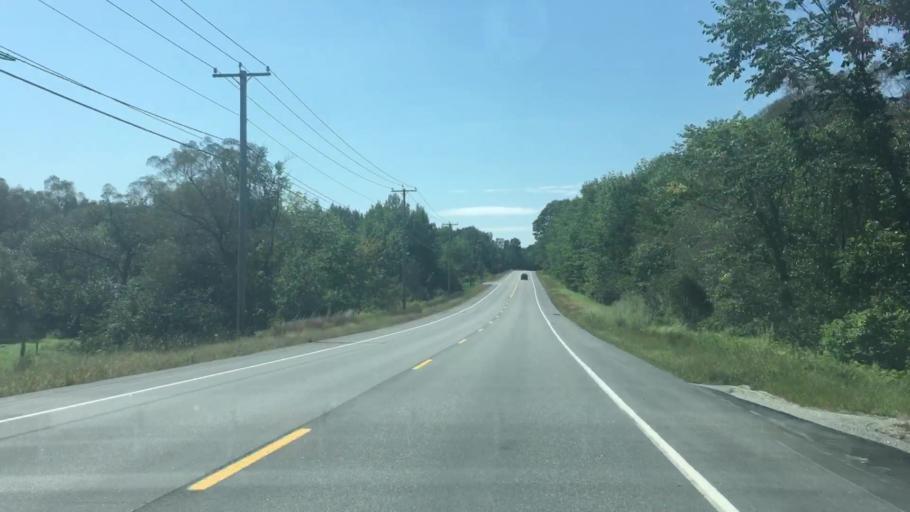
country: US
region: Maine
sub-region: Androscoggin County
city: Sabattus
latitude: 44.1263
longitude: -70.0735
